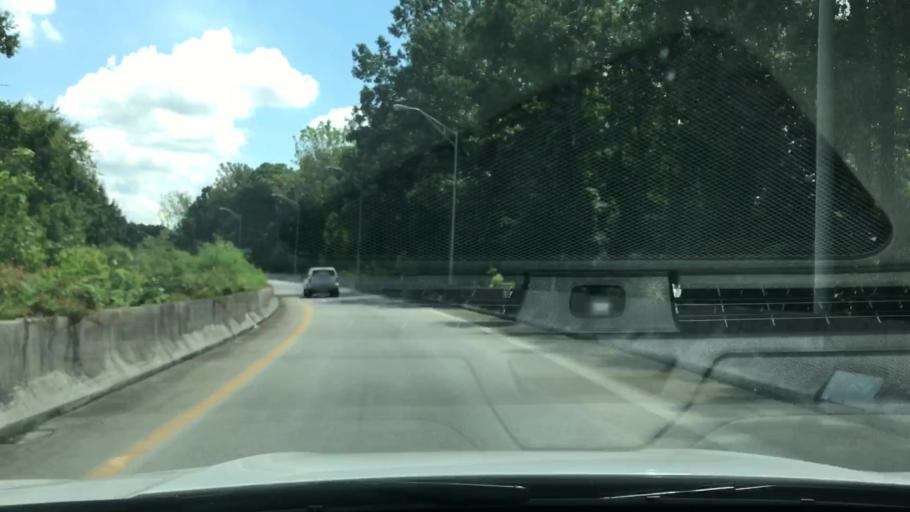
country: US
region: South Carolina
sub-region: Charleston County
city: North Charleston
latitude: 32.8933
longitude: -79.9889
